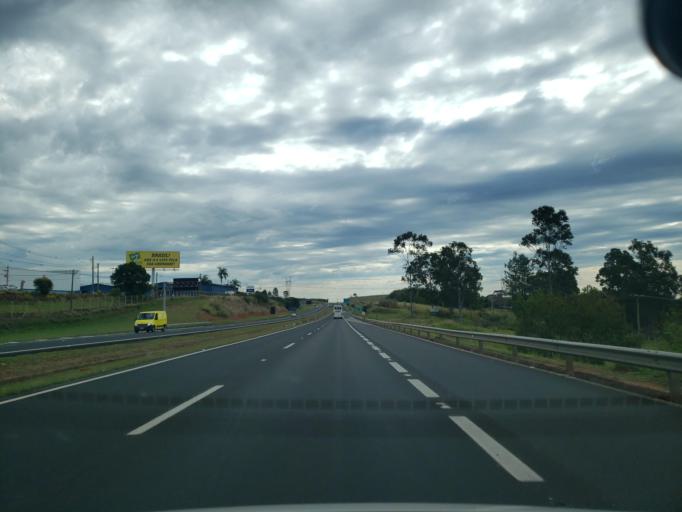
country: BR
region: Sao Paulo
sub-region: Bauru
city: Bauru
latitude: -22.2786
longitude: -49.0901
